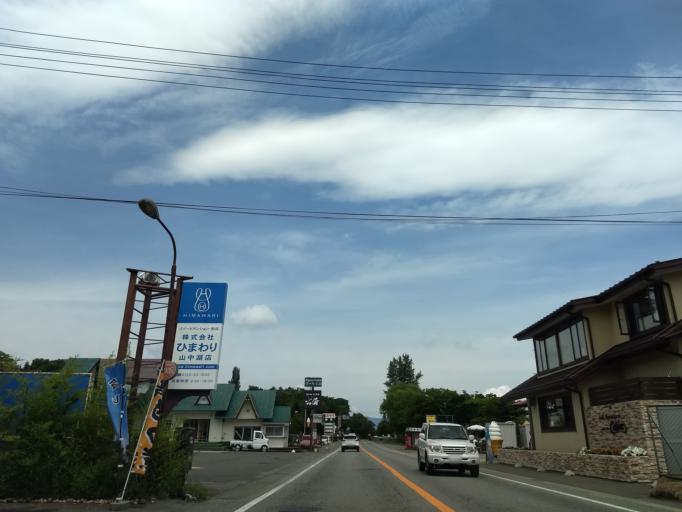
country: JP
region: Shizuoka
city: Gotemba
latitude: 35.4147
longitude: 138.8591
